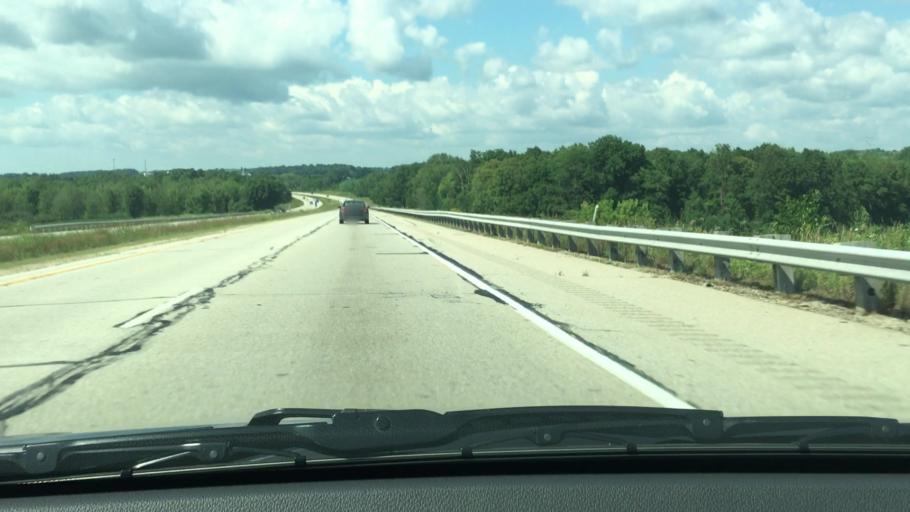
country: US
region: Wisconsin
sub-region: Dodge County
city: Theresa
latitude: 43.4972
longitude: -88.3668
